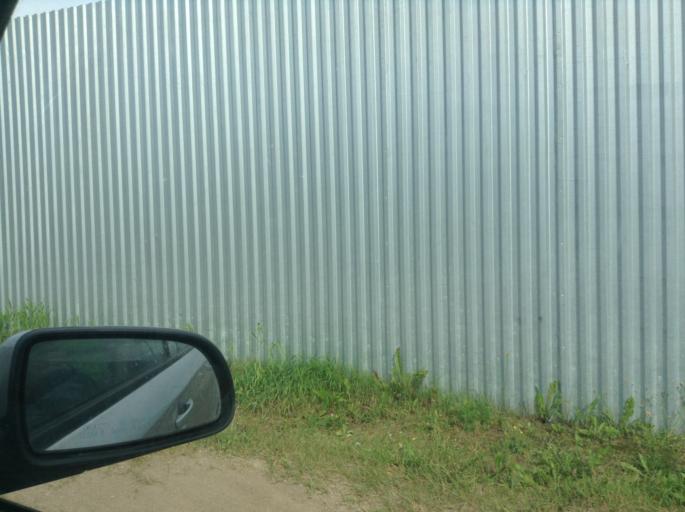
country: RU
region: Moskovskaya
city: Yegor'yevsk
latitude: 55.3647
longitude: 39.0967
